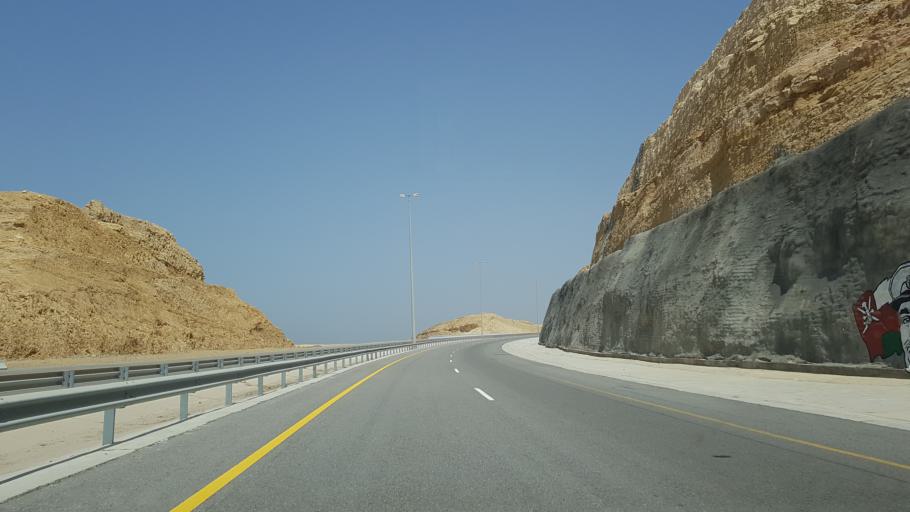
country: OM
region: Muhafazat Masqat
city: Muscat
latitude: 23.2092
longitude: 58.8893
